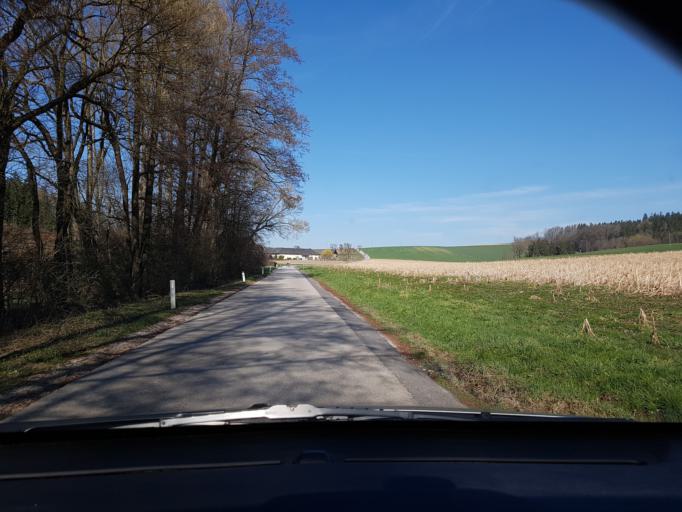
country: AT
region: Upper Austria
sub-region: Politischer Bezirk Linz-Land
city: Ansfelden
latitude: 48.1897
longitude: 14.3276
